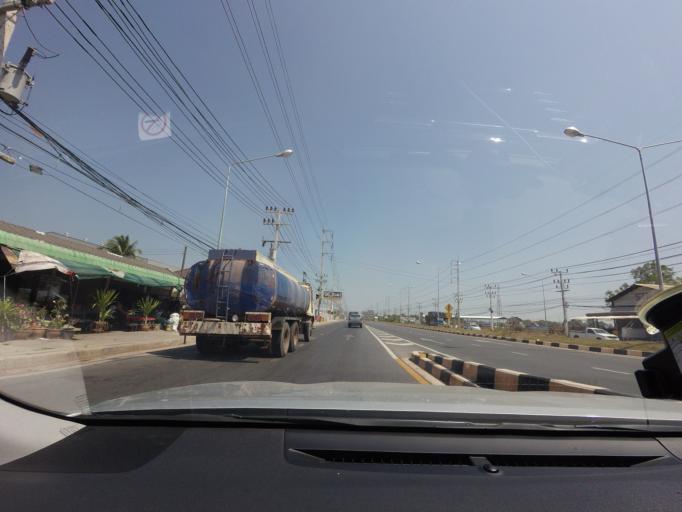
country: TH
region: Surat Thani
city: Surat Thani
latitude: 9.1568
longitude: 99.3701
